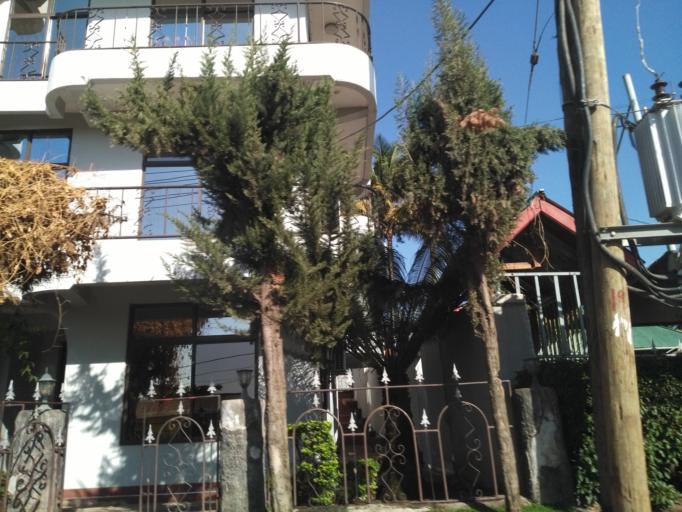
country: TZ
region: Mwanza
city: Mwanza
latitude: -2.5038
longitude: 32.8948
